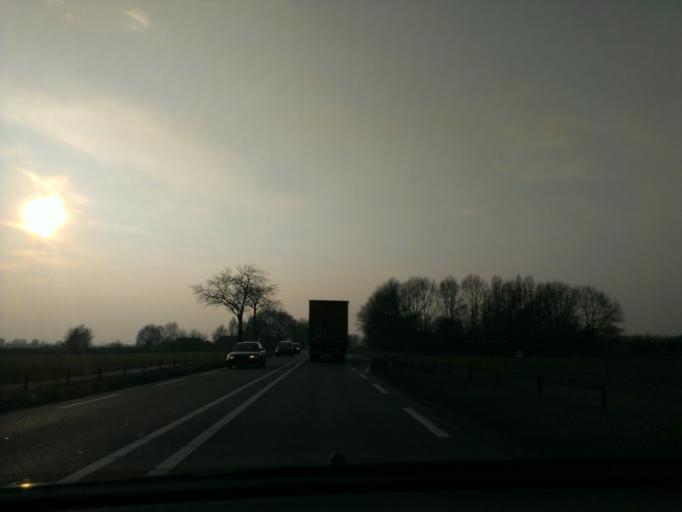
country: NL
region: Overijssel
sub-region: Gemeente Zwolle
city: Zwolle
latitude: 52.5243
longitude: 6.1717
